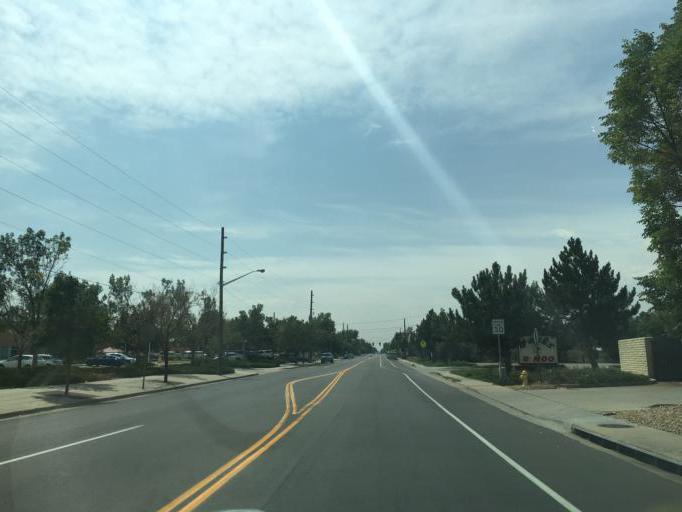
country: US
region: Colorado
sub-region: Adams County
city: Aurora
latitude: 39.7398
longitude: -104.8006
